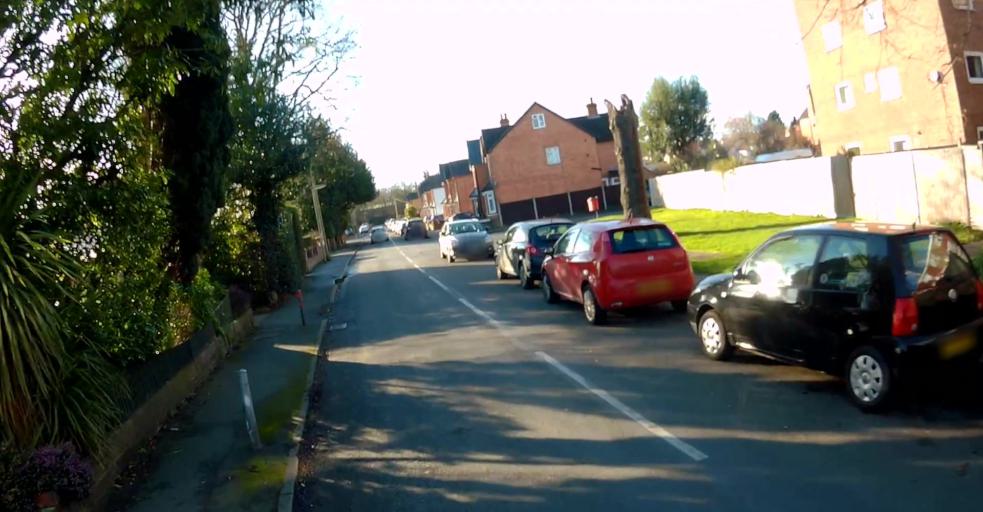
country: GB
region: England
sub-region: Surrey
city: Addlestone
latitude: 51.3669
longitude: -0.4993
